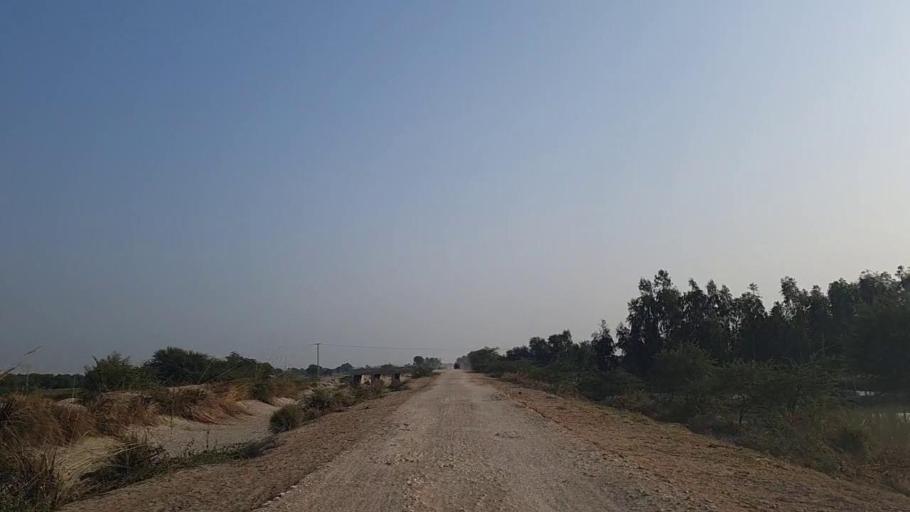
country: PK
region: Sindh
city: Jam Sahib
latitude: 26.2314
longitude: 68.5954
